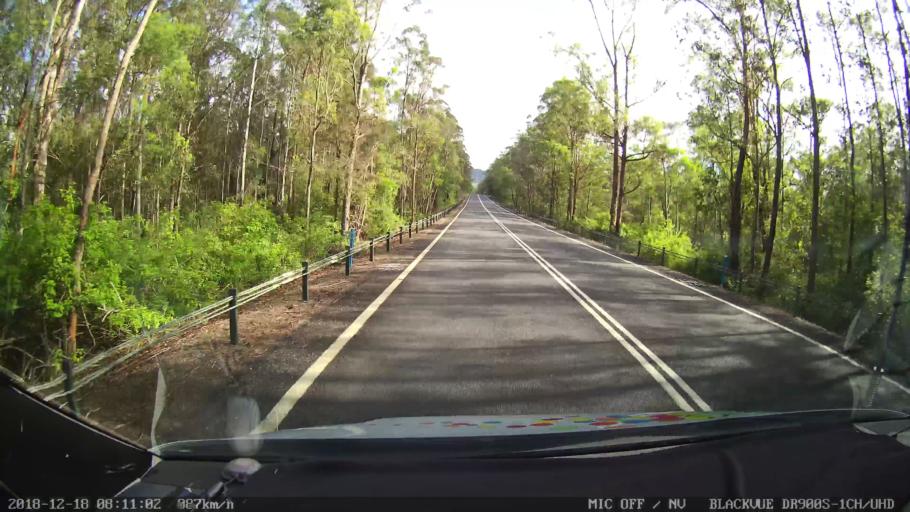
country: AU
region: New South Wales
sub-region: Kyogle
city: Kyogle
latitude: -28.3557
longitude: 152.6668
